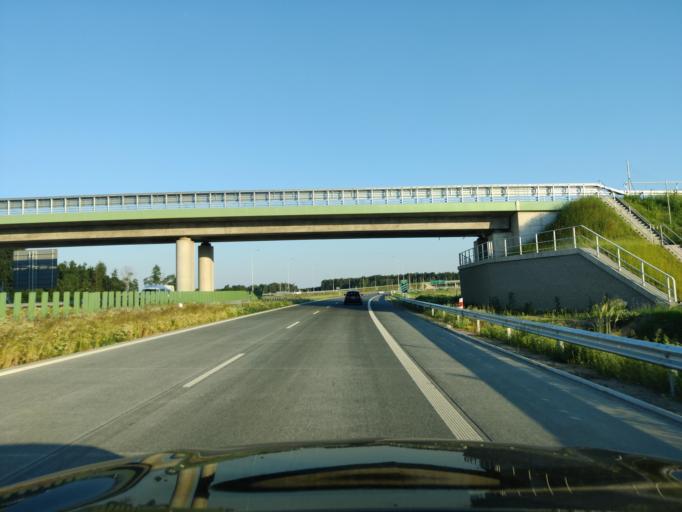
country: PL
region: Masovian Voivodeship
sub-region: Powiat mlawski
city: Strzegowo
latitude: 52.8656
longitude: 20.2860
